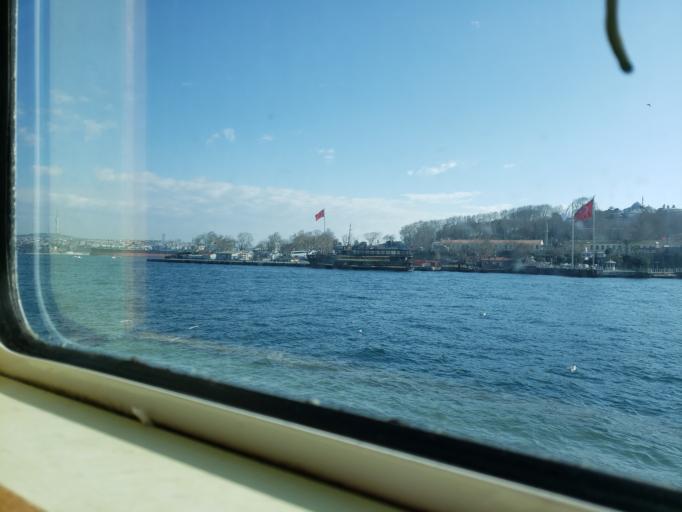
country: TR
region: Istanbul
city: Eminoenue
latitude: 41.0183
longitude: 28.9807
